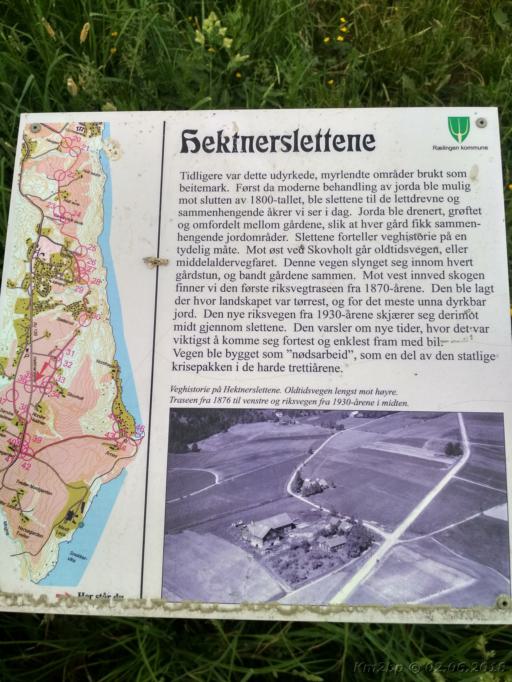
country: NO
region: Akershus
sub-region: Raelingen
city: Fjerdingby
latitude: 59.8954
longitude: 11.0983
